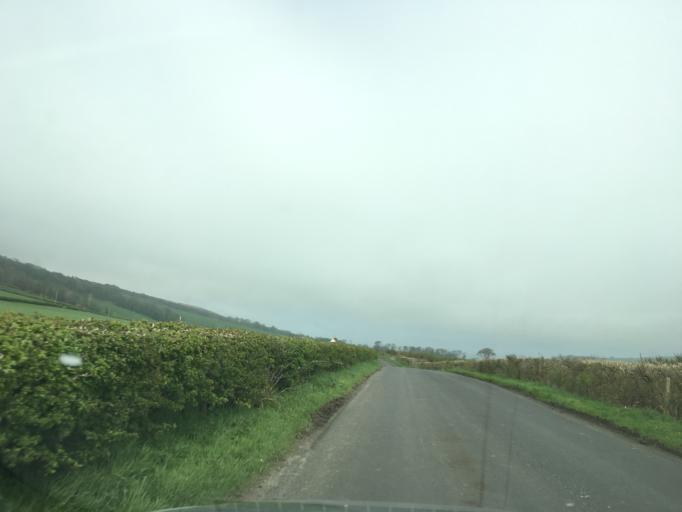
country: GB
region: Scotland
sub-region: Argyll and Bute
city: Port Bannatyne
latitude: 55.8528
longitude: -5.1359
